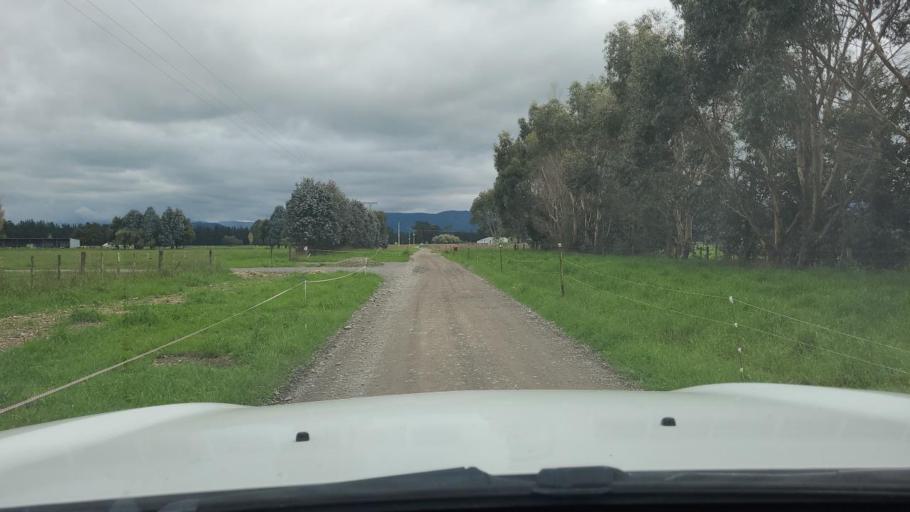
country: NZ
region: Wellington
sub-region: Masterton District
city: Masterton
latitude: -41.1269
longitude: 175.4233
